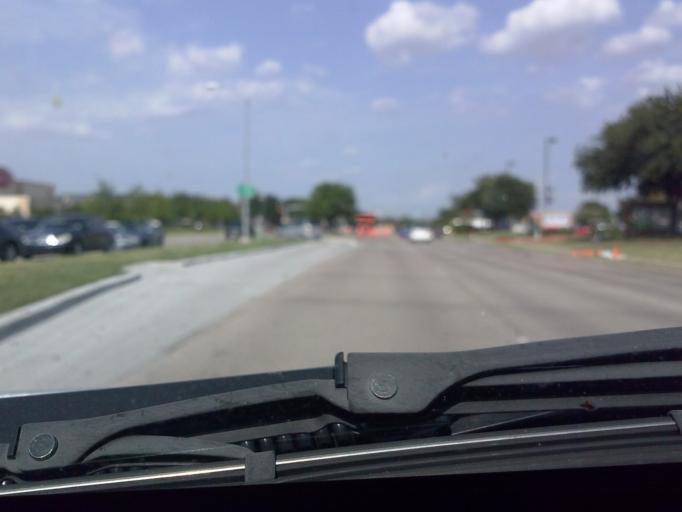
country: US
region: Texas
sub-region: Denton County
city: The Colony
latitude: 33.0451
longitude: -96.8289
